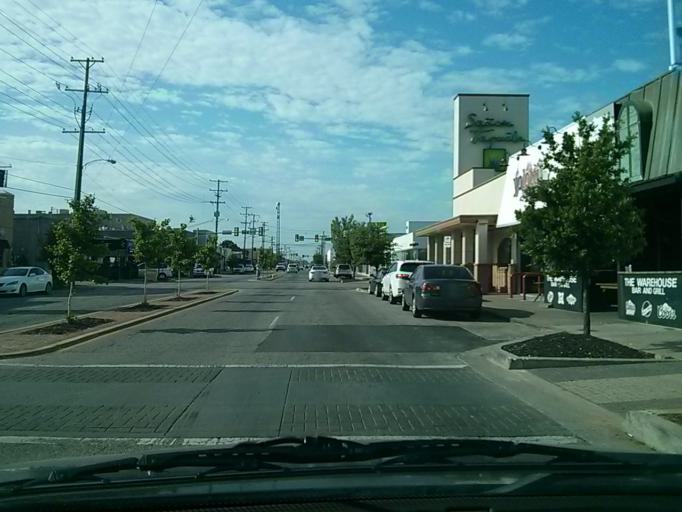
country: US
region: Oklahoma
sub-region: Tulsa County
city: Tulsa
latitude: 36.1143
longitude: -95.9758
